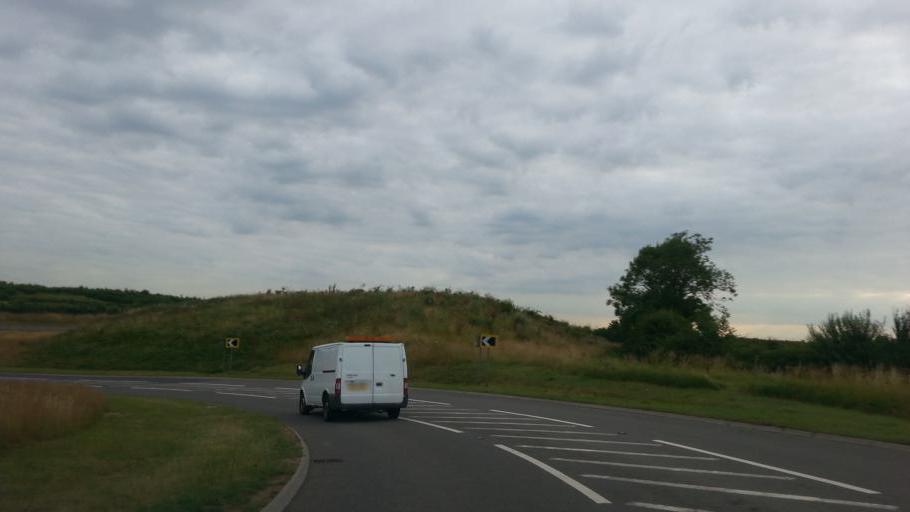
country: GB
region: England
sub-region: Nottinghamshire
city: Farndon
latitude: 53.0271
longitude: -0.8815
